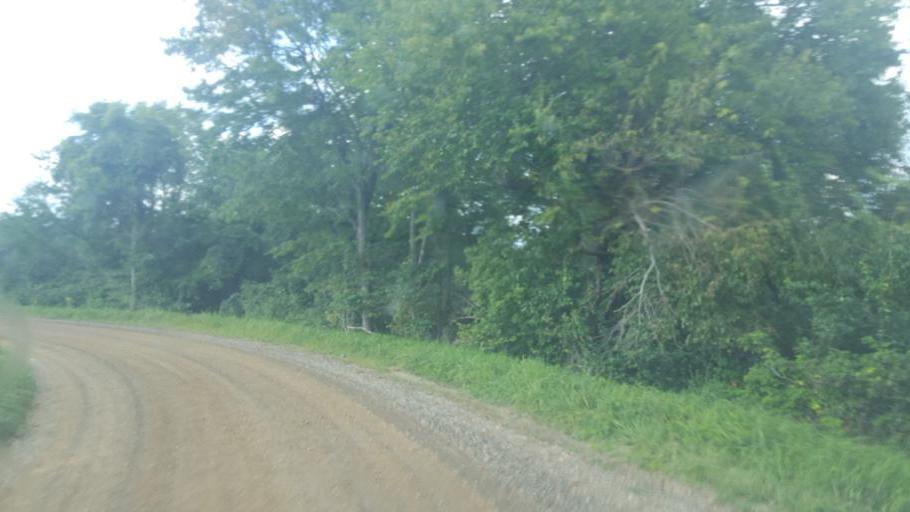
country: US
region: Ohio
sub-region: Knox County
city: Oak Hill
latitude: 40.4026
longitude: -82.2306
